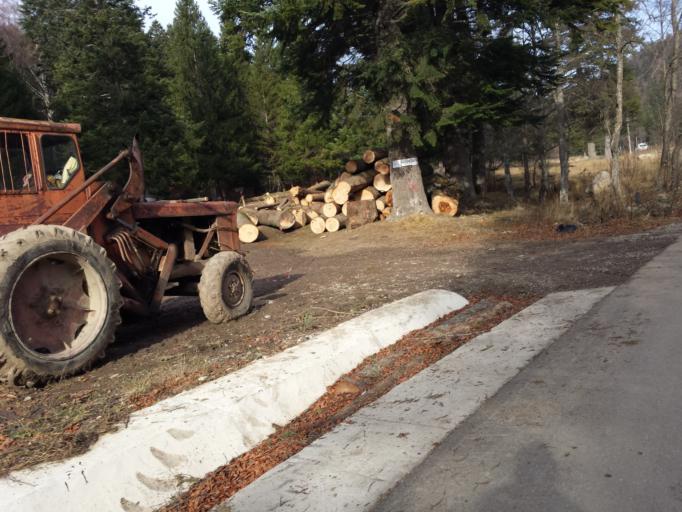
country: RO
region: Prahova
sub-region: Oras Azuga
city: Azuga
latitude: 45.4352
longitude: 25.5295
